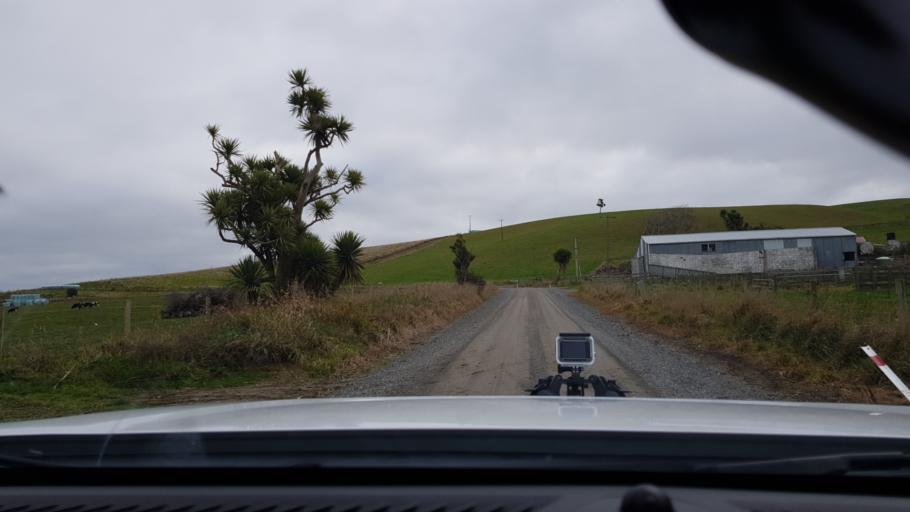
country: NZ
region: Otago
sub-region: Clutha District
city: Balclutha
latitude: -46.3225
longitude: 169.8530
